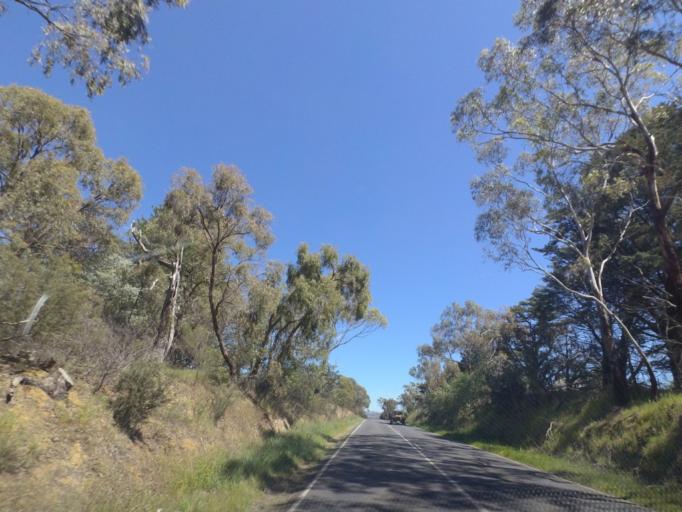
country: AU
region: Victoria
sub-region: Whittlesea
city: Whittlesea
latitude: -37.2916
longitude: 144.9111
